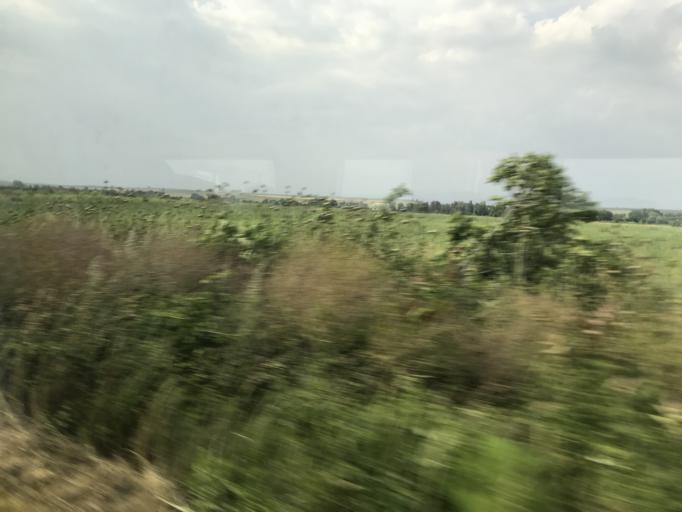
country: GR
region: East Macedonia and Thrace
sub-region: Nomos Rodopis
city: Lykeio
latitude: 41.0412
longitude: 25.6579
